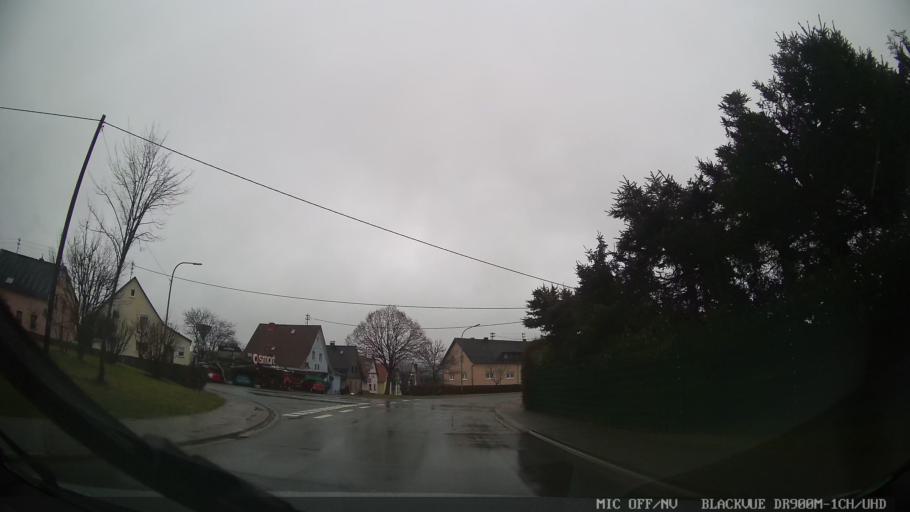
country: DE
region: Rheinland-Pfalz
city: Neuhutten
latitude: 49.5993
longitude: 7.0236
